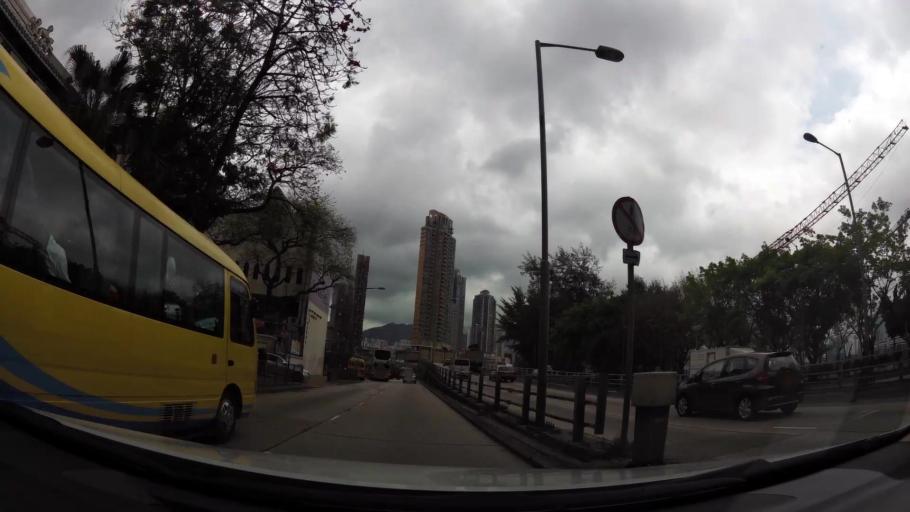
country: HK
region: Kowloon City
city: Kowloon
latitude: 22.3255
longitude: 114.1892
